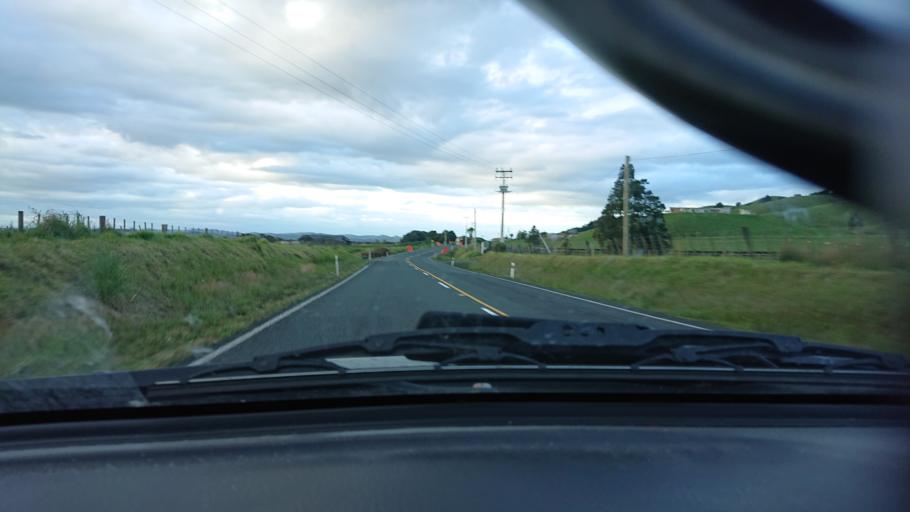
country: NZ
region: Auckland
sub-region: Auckland
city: Wellsford
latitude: -36.4530
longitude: 174.4347
